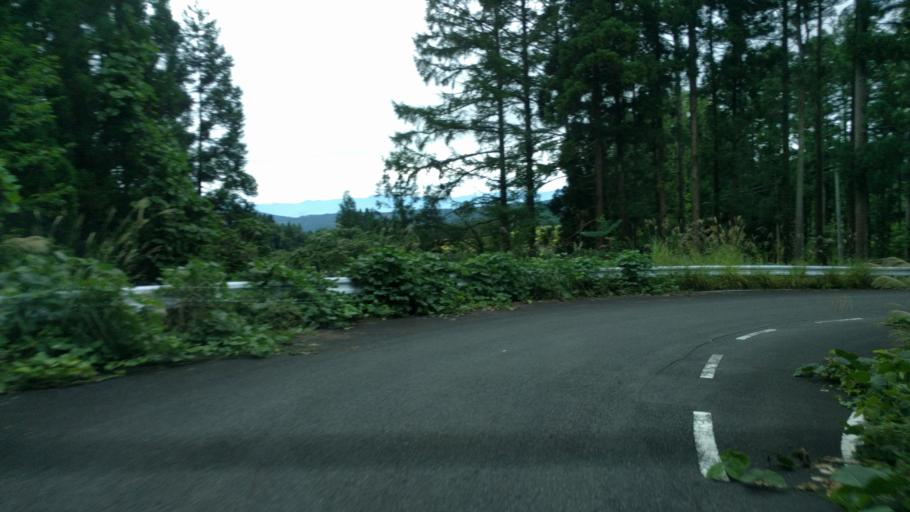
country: JP
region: Fukushima
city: Kitakata
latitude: 37.5394
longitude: 139.7299
